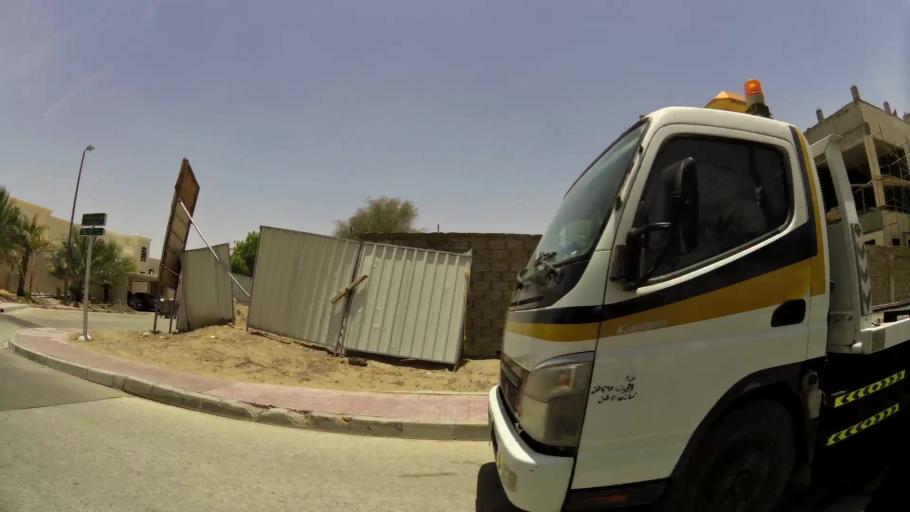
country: OM
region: Al Buraimi
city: Al Buraymi
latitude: 24.2635
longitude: 55.7352
